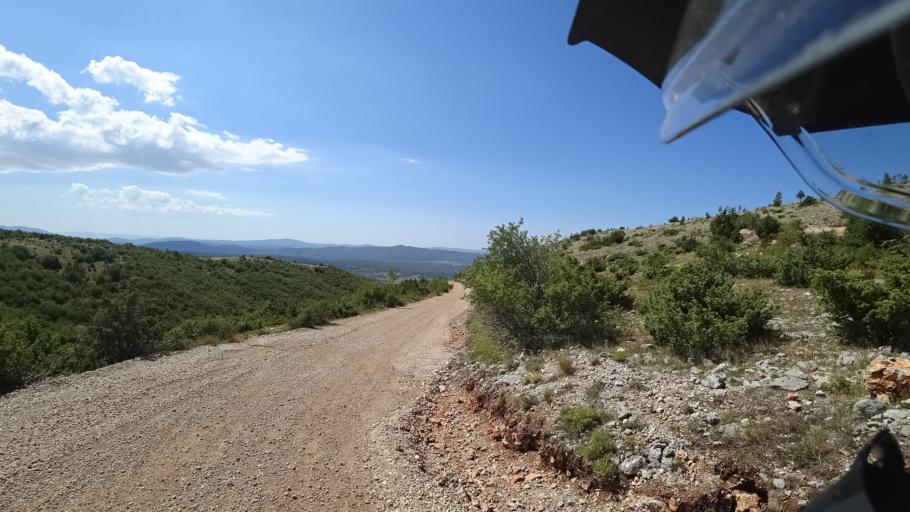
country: HR
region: Splitsko-Dalmatinska
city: Hrvace
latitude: 43.7622
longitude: 16.4691
